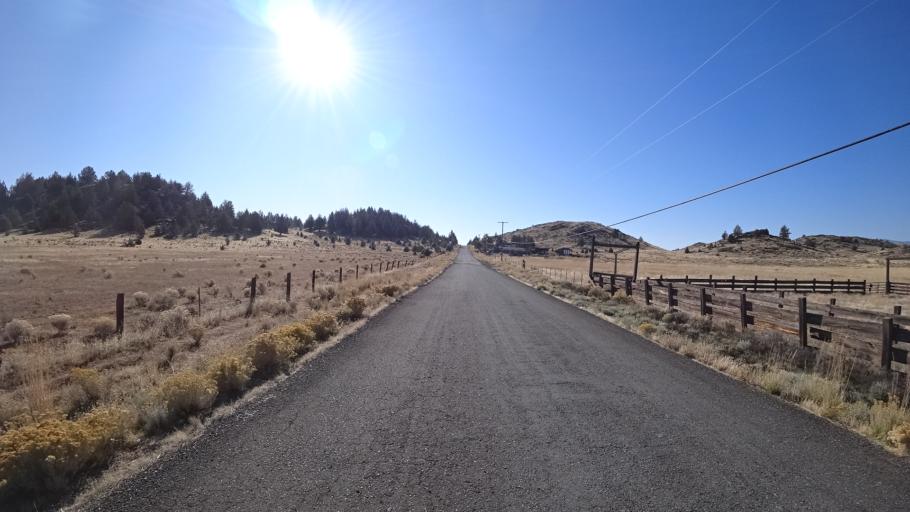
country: US
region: California
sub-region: Siskiyou County
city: Montague
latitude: 41.7017
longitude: -122.4377
